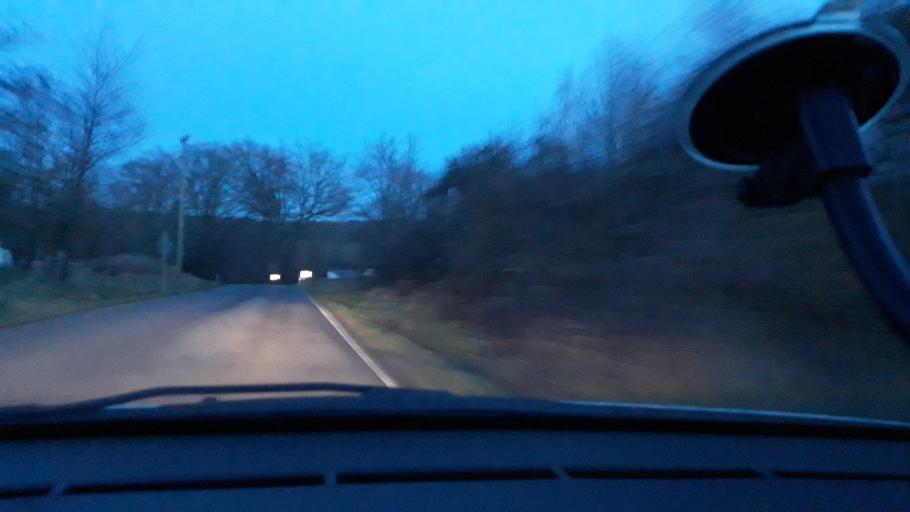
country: DE
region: Saarland
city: Blieskastel
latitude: 49.2109
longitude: 7.2427
